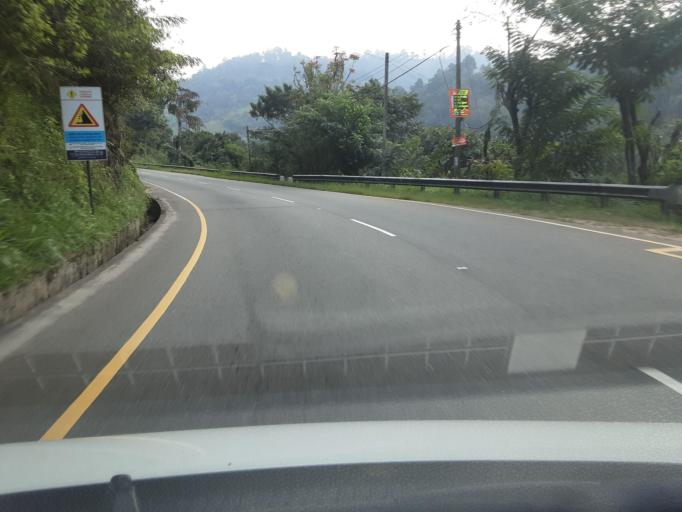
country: LK
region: Uva
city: Badulla
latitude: 6.9466
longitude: 81.0177
